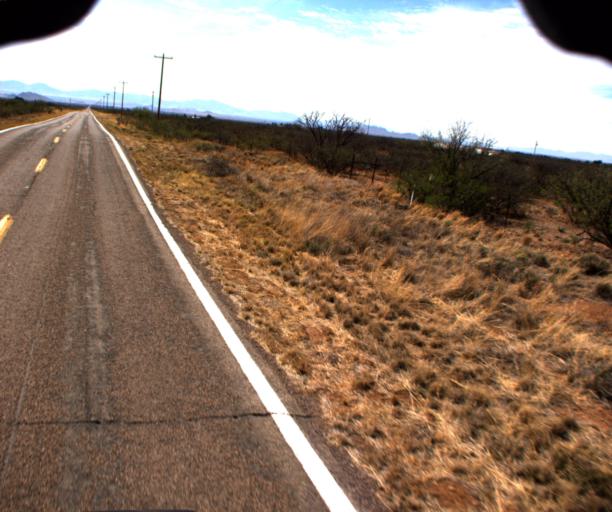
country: US
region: Arizona
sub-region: Cochise County
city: Willcox
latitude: 31.8760
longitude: -109.5188
